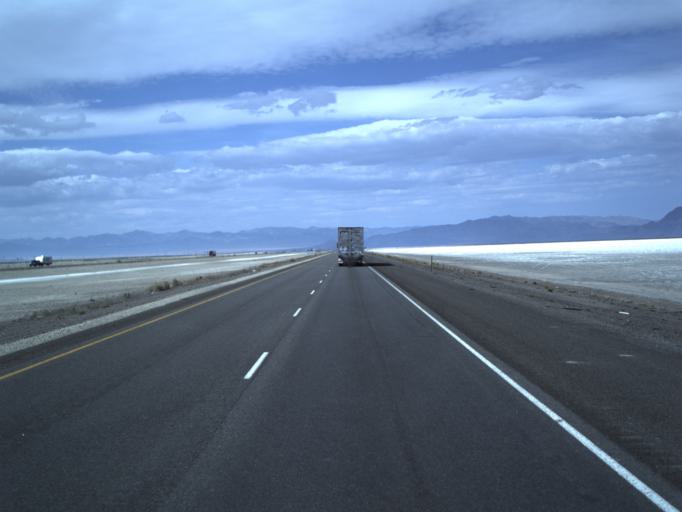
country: US
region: Utah
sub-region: Tooele County
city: Wendover
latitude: 40.7382
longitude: -113.7898
